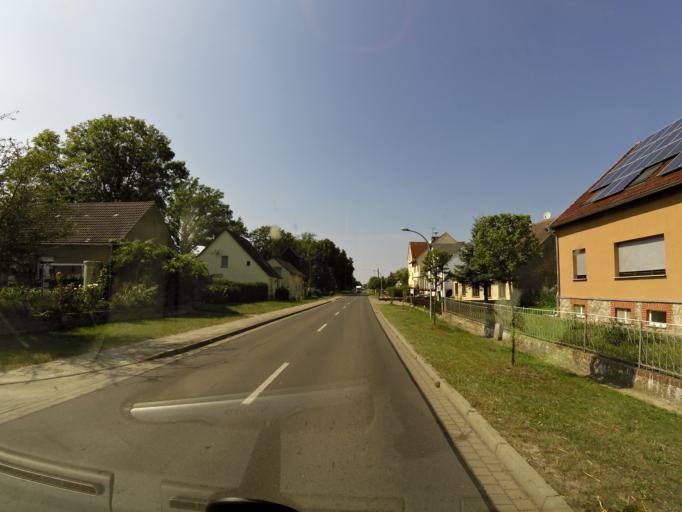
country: DE
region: Brandenburg
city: Zehdenick
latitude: 53.0104
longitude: 13.2892
